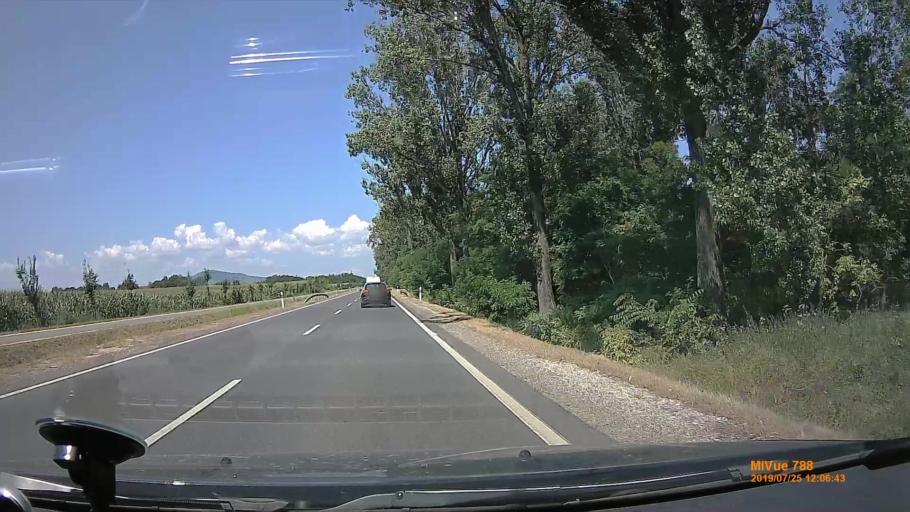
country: HU
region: Szabolcs-Szatmar-Bereg
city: Tiszanagyfalu
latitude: 48.0754
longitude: 21.5150
